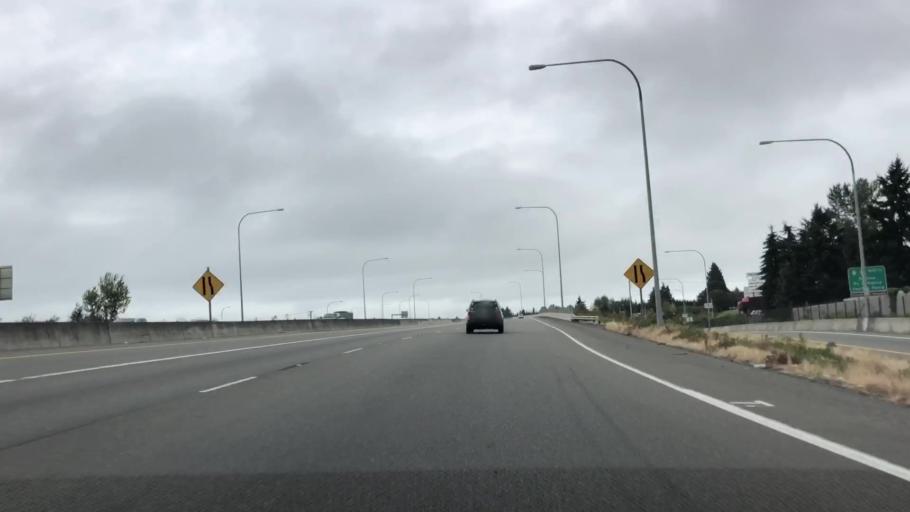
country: US
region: Washington
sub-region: Pierce County
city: Fircrest
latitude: 47.2526
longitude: -122.5130
